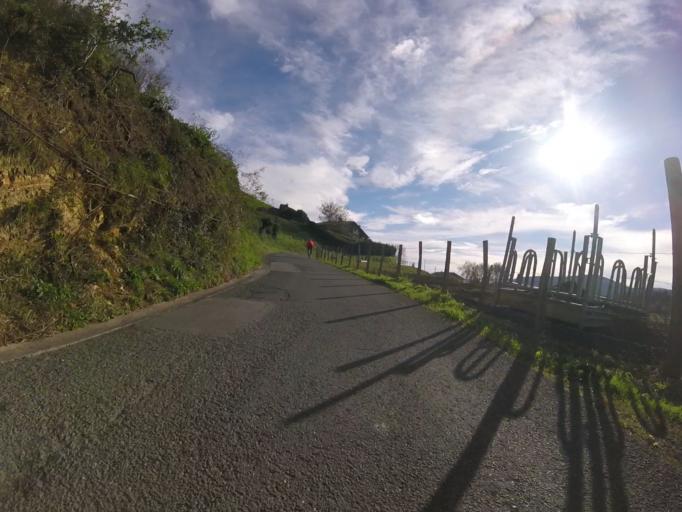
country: ES
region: Basque Country
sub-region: Provincia de Guipuzcoa
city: Orio
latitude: 43.2878
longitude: -2.1012
